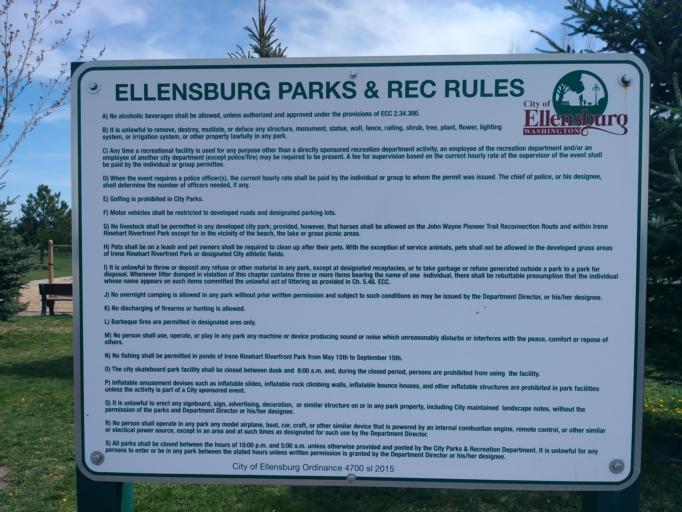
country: US
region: Washington
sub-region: Kittitas County
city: Ellensburg
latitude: 46.9926
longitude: -120.5654
